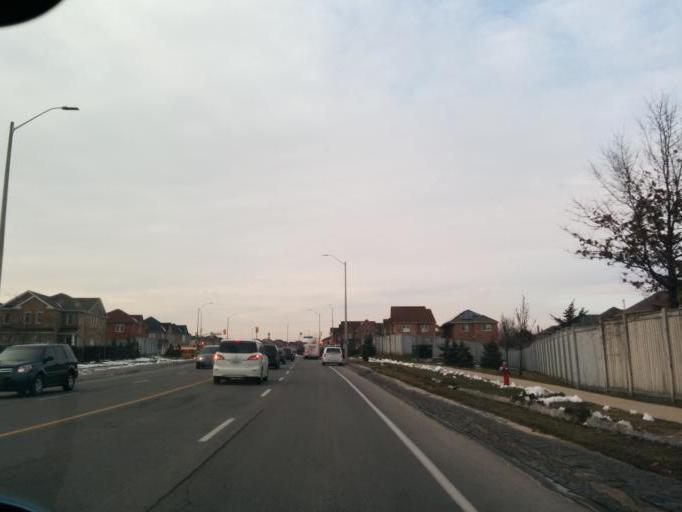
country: CA
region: Ontario
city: Mississauga
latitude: 43.5938
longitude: -79.6568
